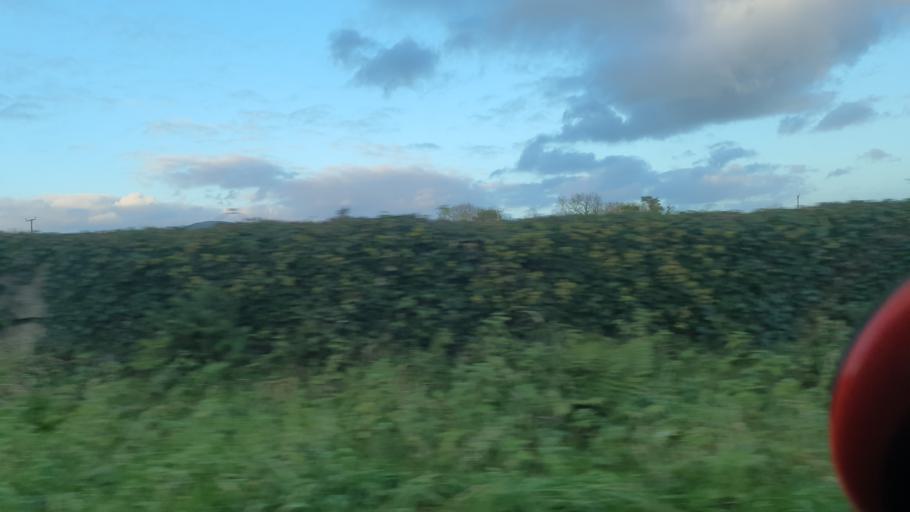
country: GB
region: Northern Ireland
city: Kilkeel
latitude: 54.0591
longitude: -6.0876
